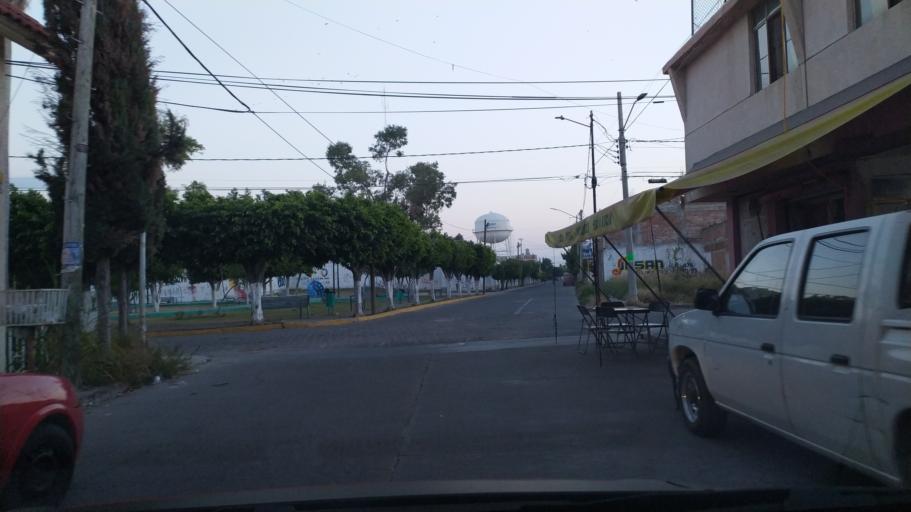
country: MX
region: Guanajuato
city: San Francisco del Rincon
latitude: 21.0102
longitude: -101.8605
